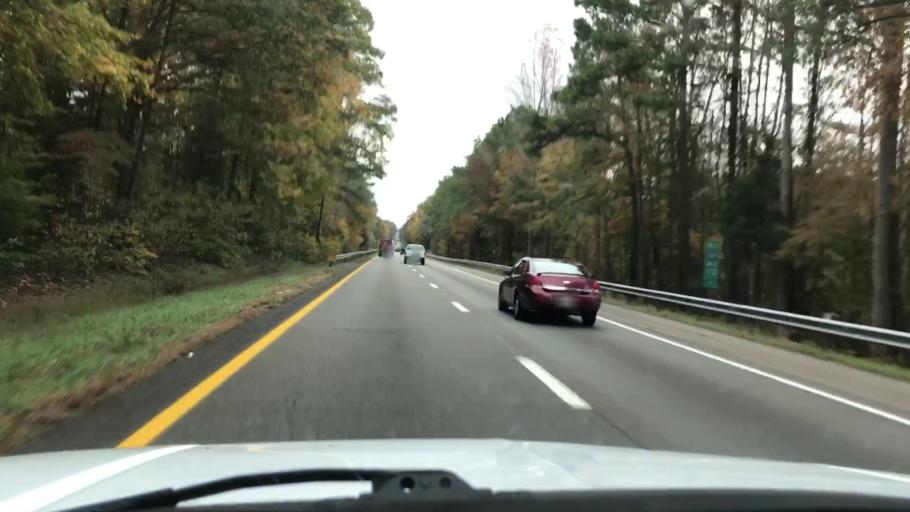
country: US
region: Virginia
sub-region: Henrico County
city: Wyndham
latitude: 37.6894
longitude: -77.6888
